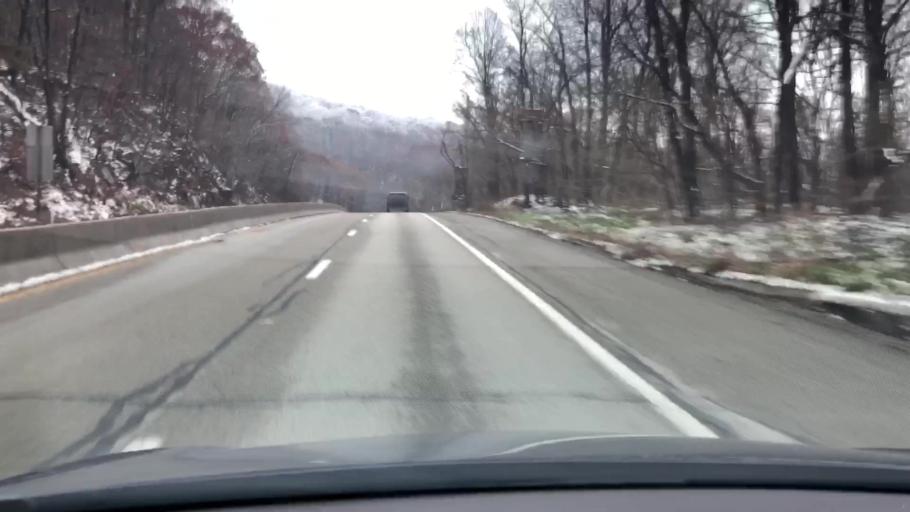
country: US
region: Pennsylvania
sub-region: Fayette County
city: Hopwood
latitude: 39.8664
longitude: -79.6854
